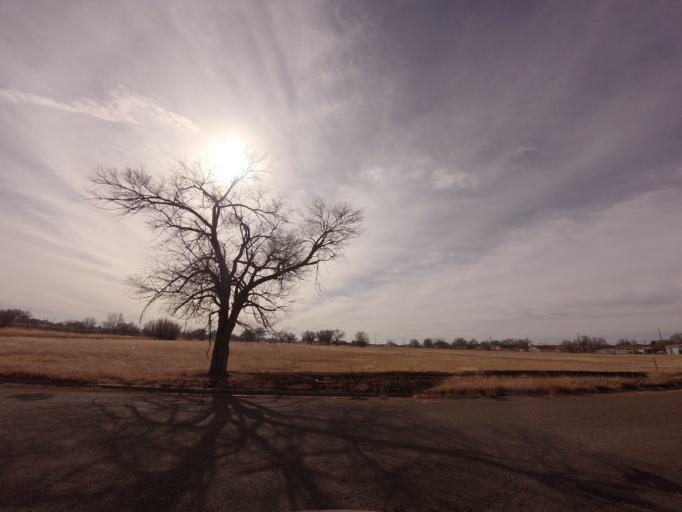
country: US
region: New Mexico
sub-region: Curry County
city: Clovis
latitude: 34.4086
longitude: -103.2353
